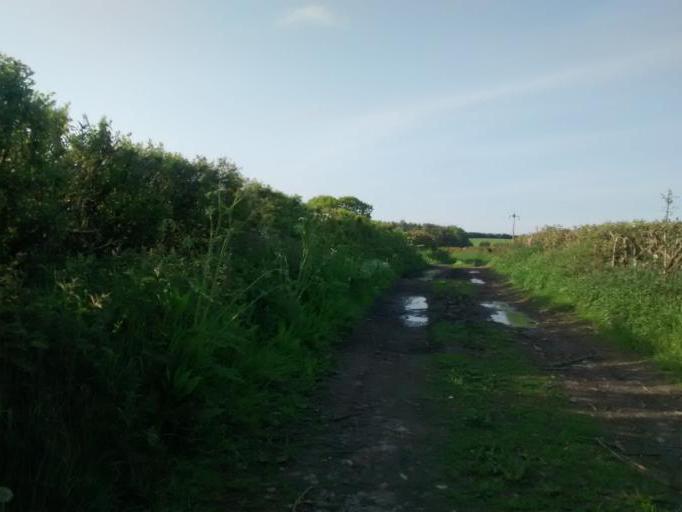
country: GB
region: England
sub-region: County Durham
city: West Cornforth
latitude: 54.7287
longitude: -1.5481
